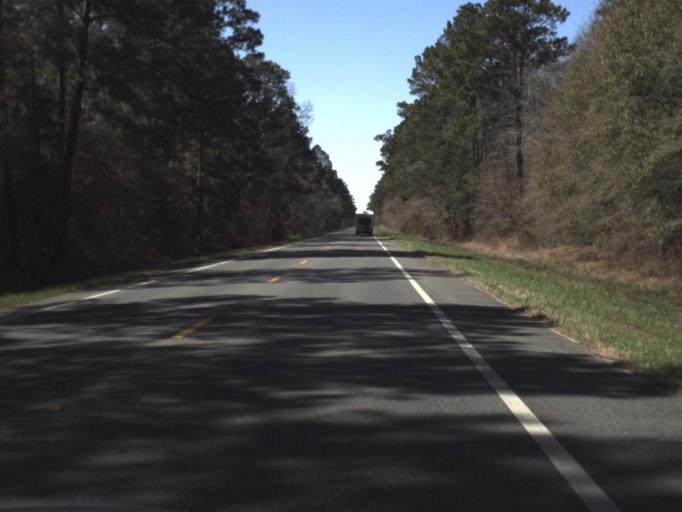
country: US
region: Florida
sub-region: Washington County
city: Chipley
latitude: 30.7917
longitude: -85.3889
